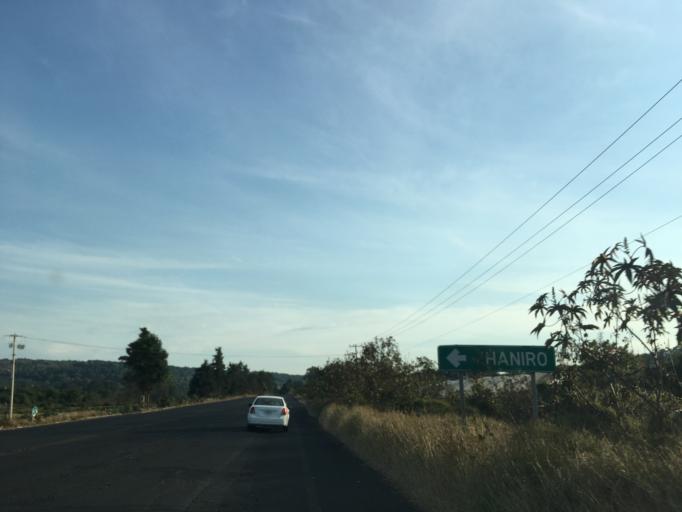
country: MX
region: Michoacan
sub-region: Tingueindin
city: Tingueindin
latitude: 19.7161
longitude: -102.4799
